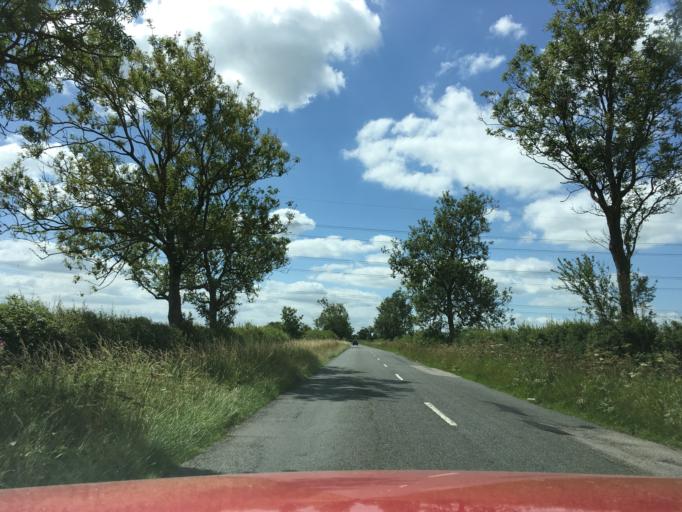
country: GB
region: England
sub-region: Buckinghamshire
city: Winslow
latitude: 51.9265
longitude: -0.8366
